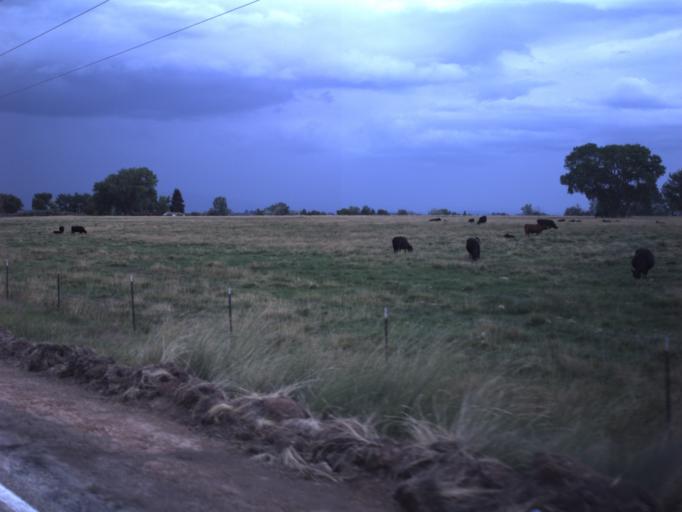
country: US
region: Utah
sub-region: Duchesne County
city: Roosevelt
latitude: 40.3639
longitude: -110.0296
